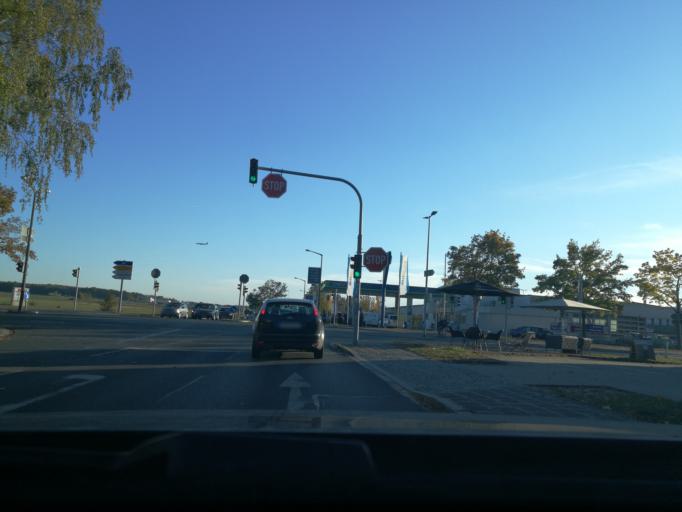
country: DE
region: Bavaria
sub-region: Regierungsbezirk Mittelfranken
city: Furth
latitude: 49.5235
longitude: 11.0074
